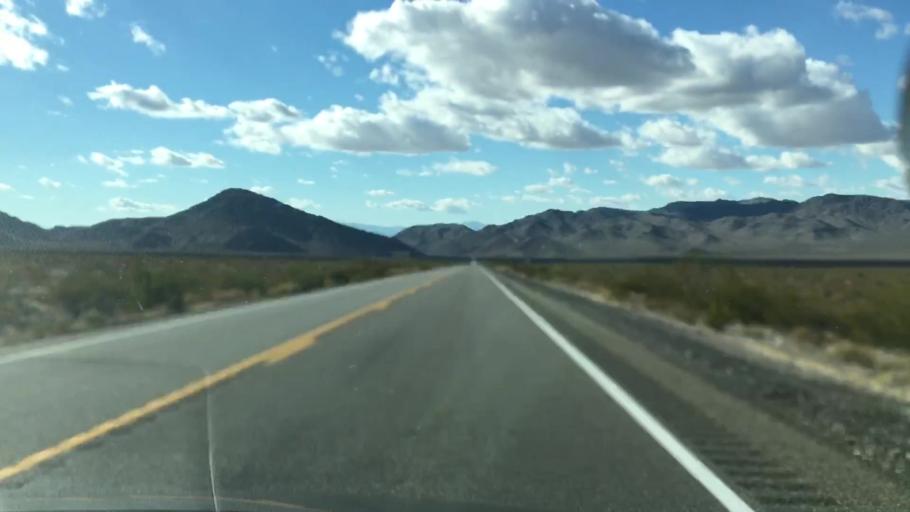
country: US
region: Nevada
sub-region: Nye County
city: Pahrump
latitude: 36.5945
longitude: -116.0172
